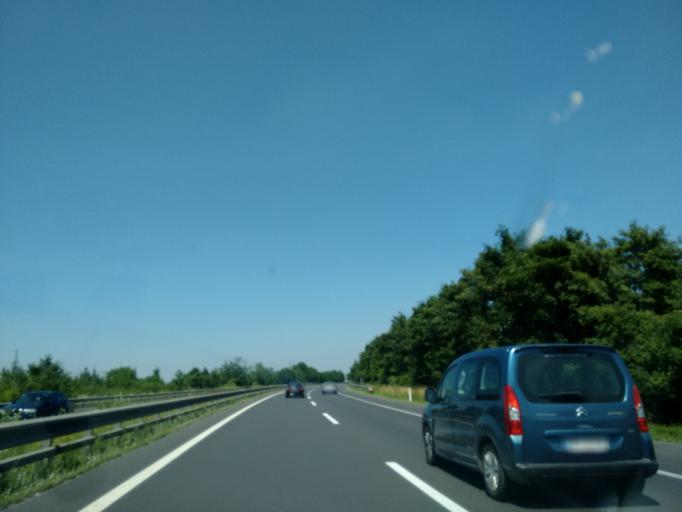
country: AT
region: Upper Austria
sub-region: Wels-Land
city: Gunskirchen
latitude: 48.1614
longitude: 13.9792
